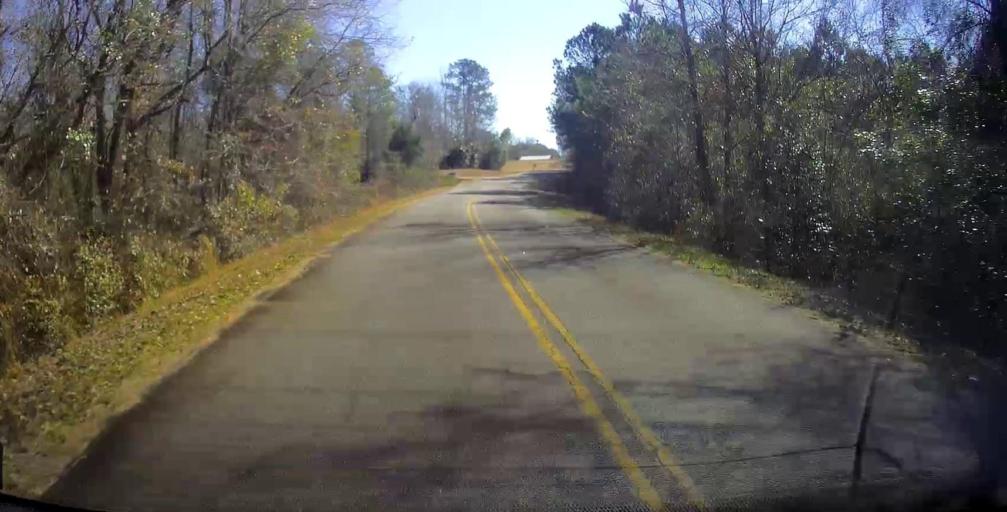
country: US
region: Georgia
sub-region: Peach County
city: Byron
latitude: 32.6207
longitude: -83.8349
